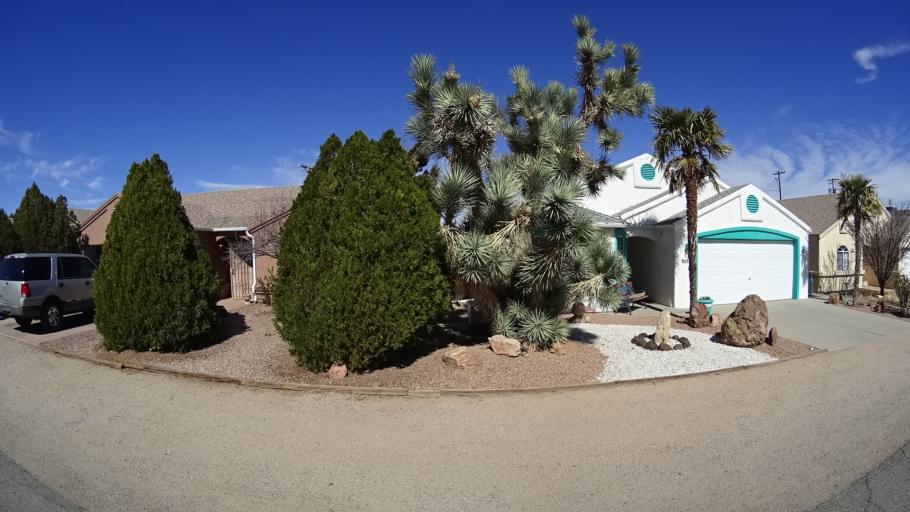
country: US
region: Arizona
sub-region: Mohave County
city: Kingman
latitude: 35.2132
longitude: -114.0371
